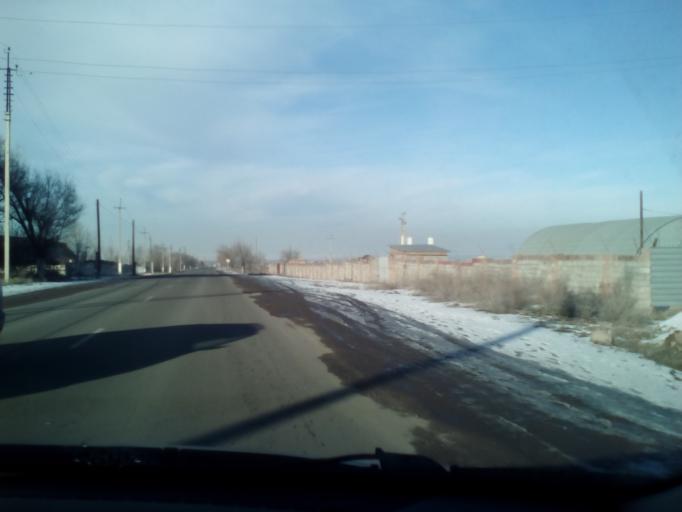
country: KZ
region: Almaty Oblysy
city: Burunday
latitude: 43.1922
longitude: 76.4148
